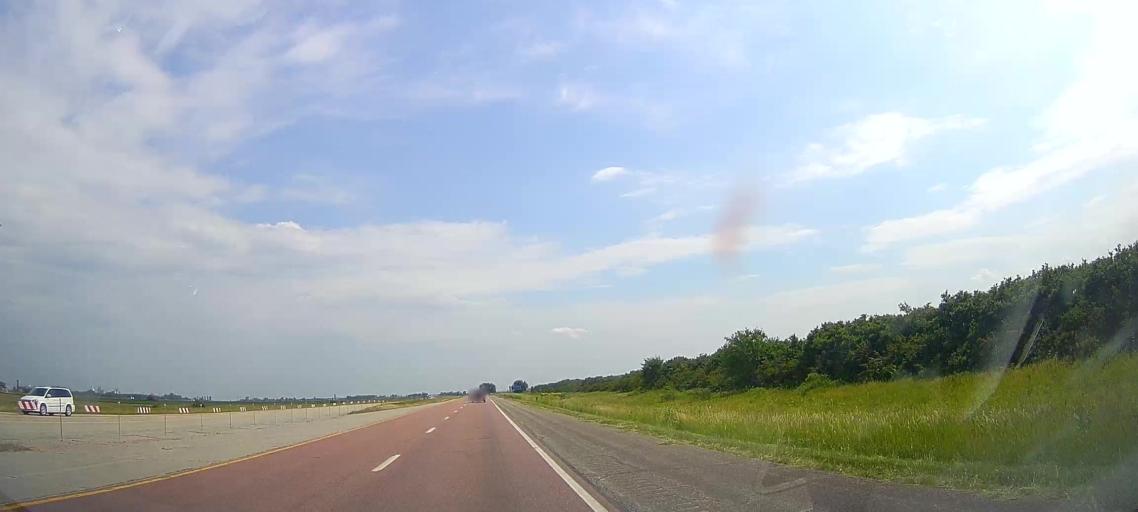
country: US
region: Iowa
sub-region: Monona County
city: Onawa
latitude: 41.9564
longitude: -96.1034
